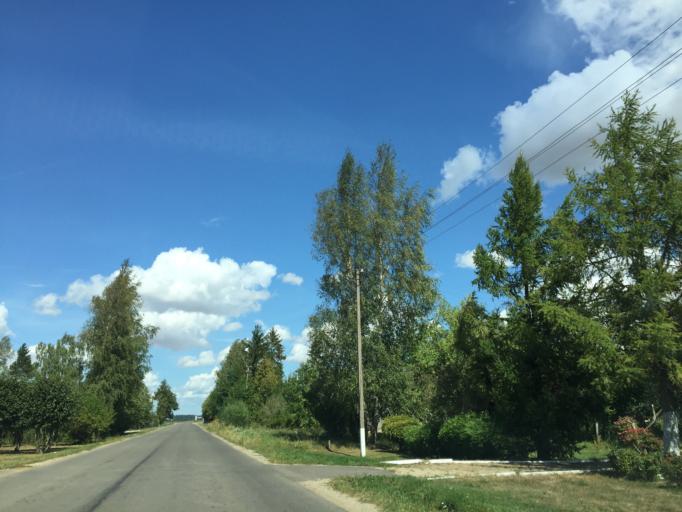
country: LV
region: Rundales
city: Pilsrundale
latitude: 56.3190
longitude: 23.9116
